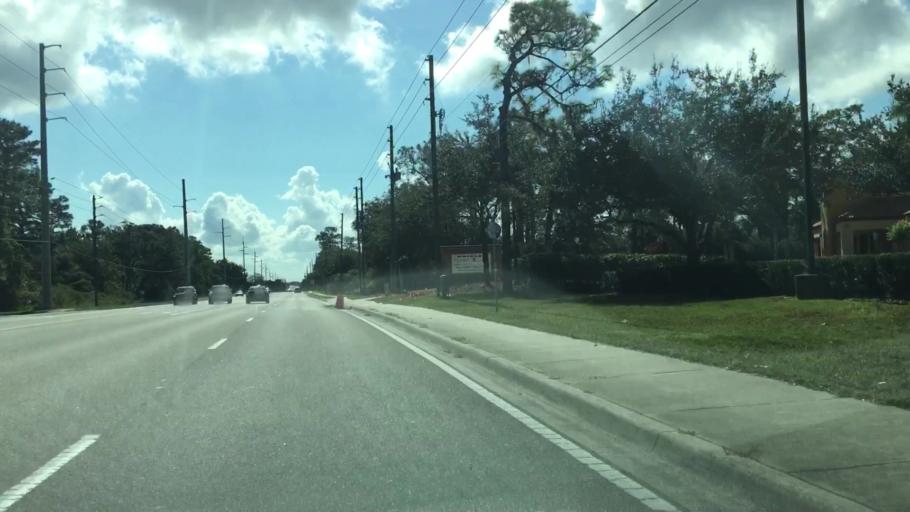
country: US
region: Florida
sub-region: Volusia County
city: Deltona
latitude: 28.9045
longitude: -81.2885
